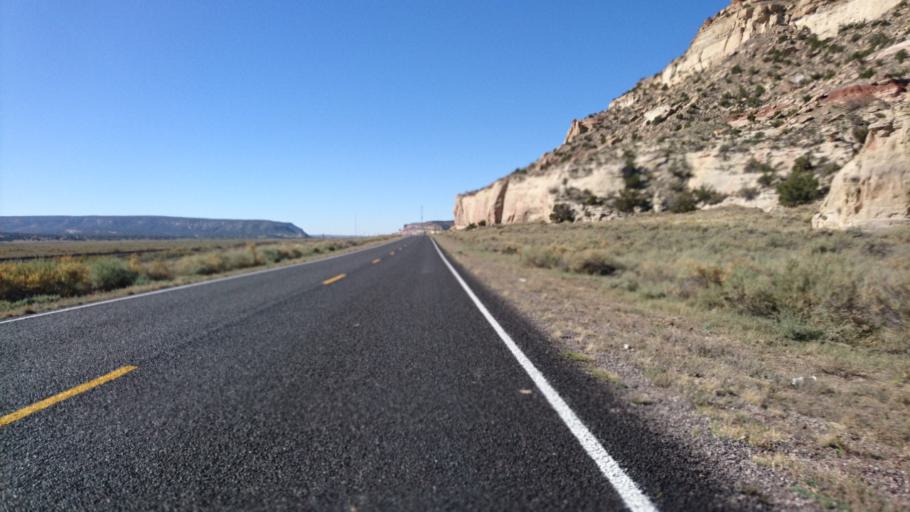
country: US
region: Arizona
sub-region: Apache County
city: Houck
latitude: 35.4047
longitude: -109.0102
